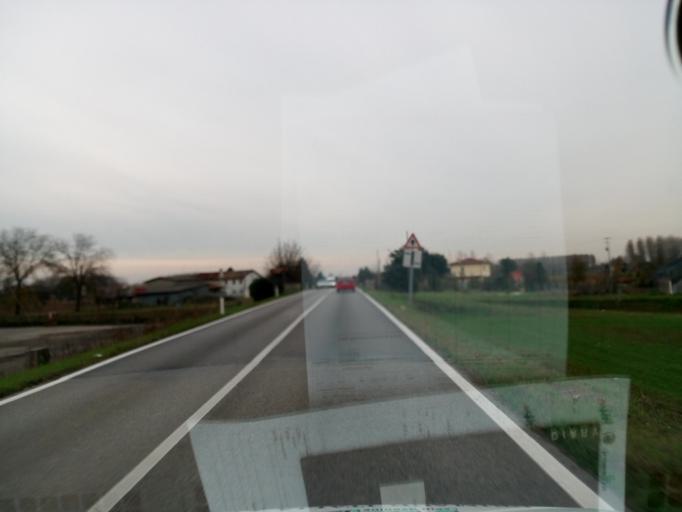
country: IT
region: Veneto
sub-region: Provincia di Padova
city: Piombino Dese
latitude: 45.5915
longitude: 12.0006
